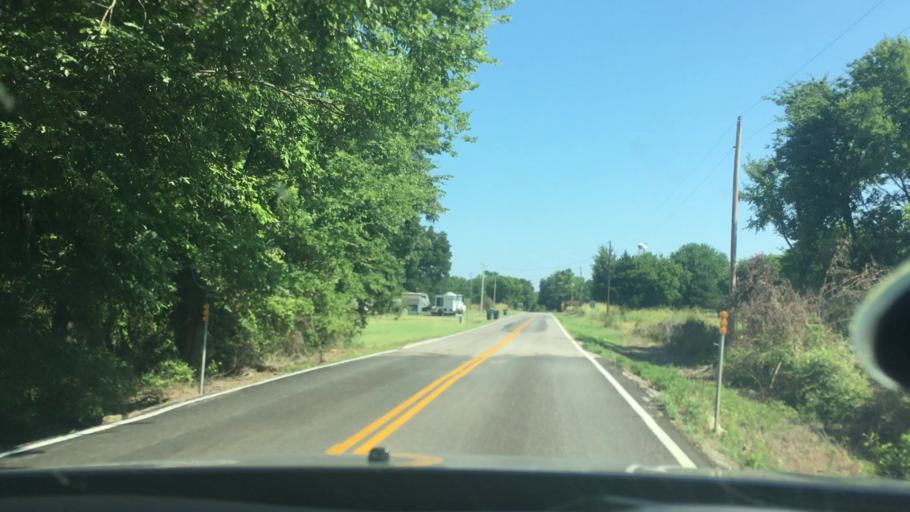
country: US
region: Oklahoma
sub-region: Johnston County
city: Tishomingo
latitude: 34.2046
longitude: -96.5428
